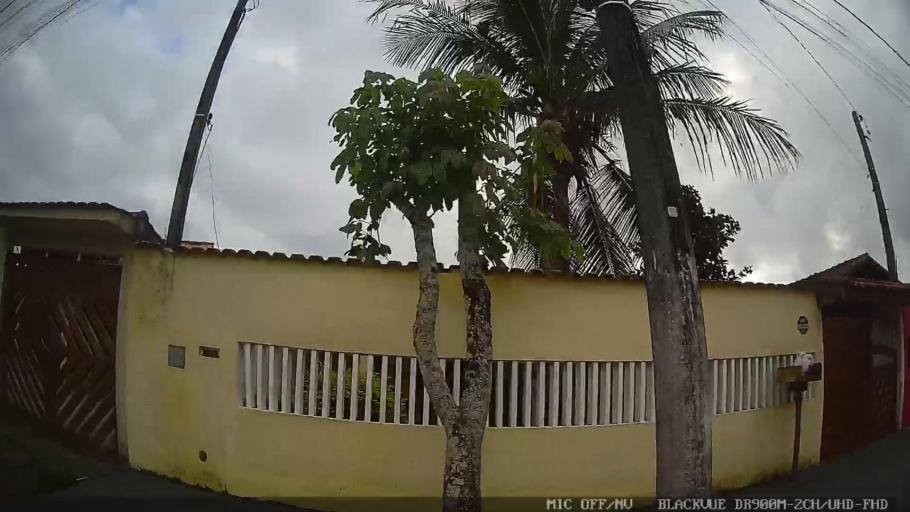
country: BR
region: Sao Paulo
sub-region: Itanhaem
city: Itanhaem
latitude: -24.1954
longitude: -46.8161
